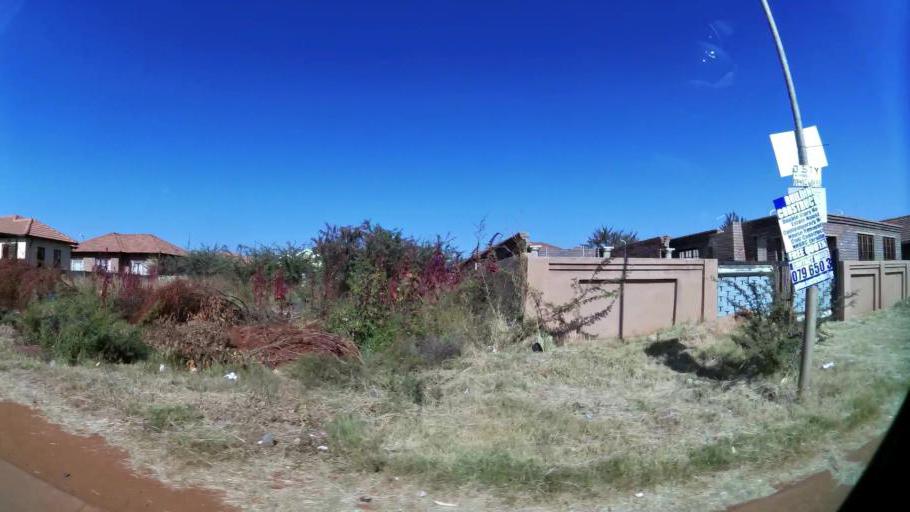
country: ZA
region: North-West
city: Ga-Rankuwa
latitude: -25.6405
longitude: 28.0892
